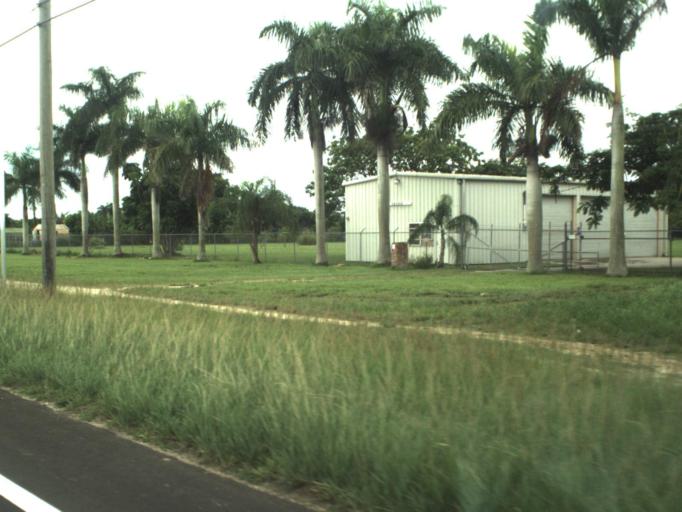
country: US
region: Florida
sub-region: Miami-Dade County
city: Country Walk
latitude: 25.6321
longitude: -80.4798
